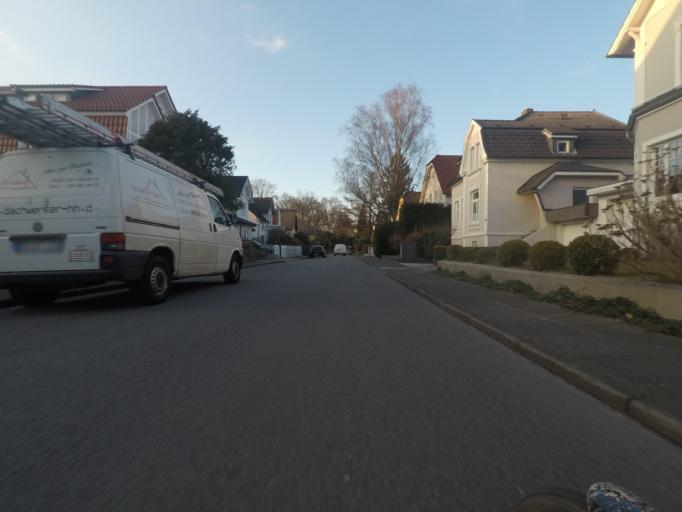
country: DE
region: Schleswig-Holstein
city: Barsbuettel
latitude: 53.6071
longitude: 10.1634
